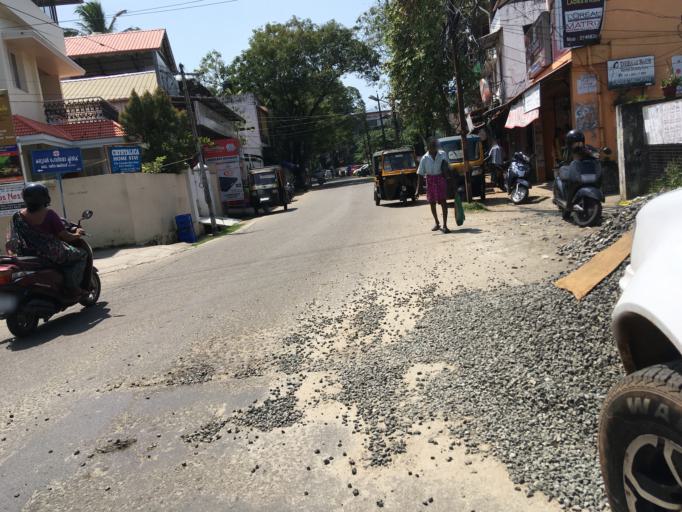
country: IN
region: Kerala
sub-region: Ernakulam
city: Cochin
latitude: 9.9604
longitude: 76.2457
